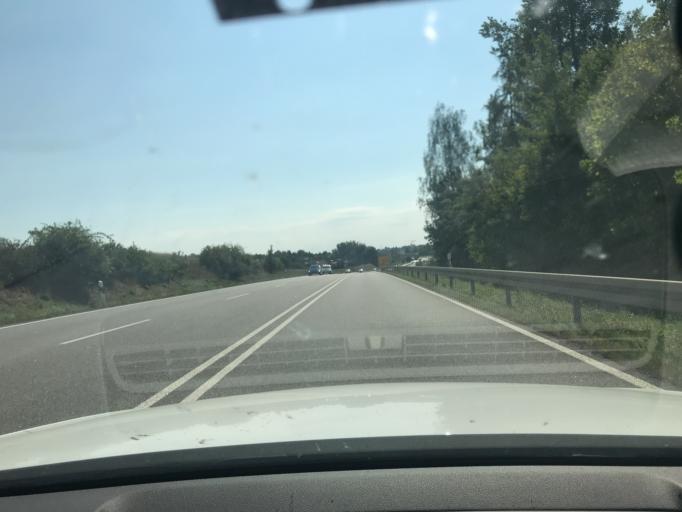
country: DE
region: Bavaria
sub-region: Upper Palatinate
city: Poppenricht
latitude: 49.4531
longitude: 11.8235
